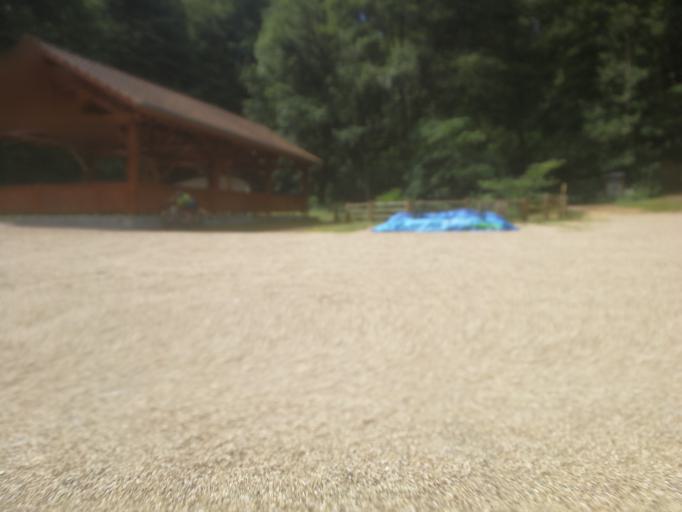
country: FR
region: Lorraine
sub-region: Departement de la Moselle
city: Rosselange
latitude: 49.2361
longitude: 6.0752
